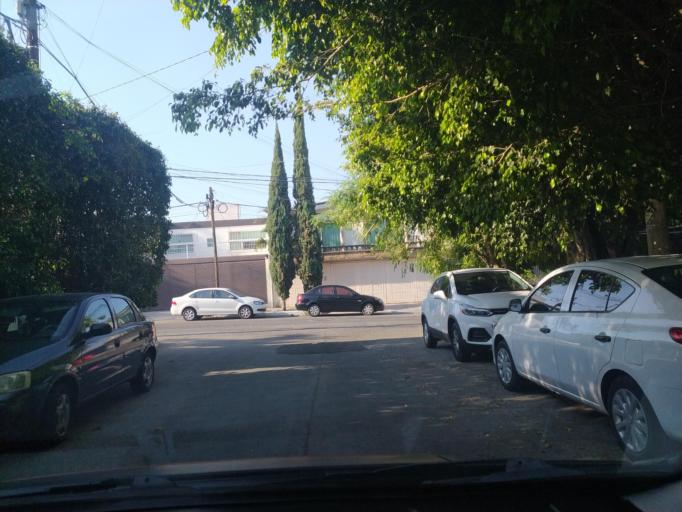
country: MX
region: Jalisco
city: Zapopan2
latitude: 20.6939
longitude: -103.3878
